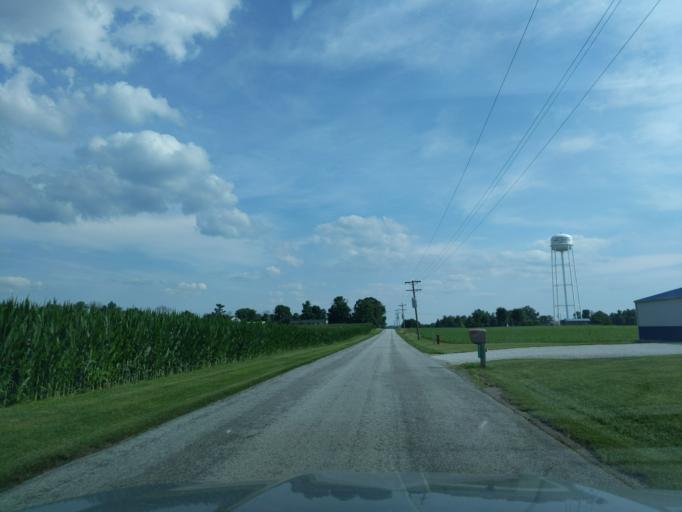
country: US
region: Indiana
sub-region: Decatur County
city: Greensburg
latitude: 39.2744
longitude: -85.4651
